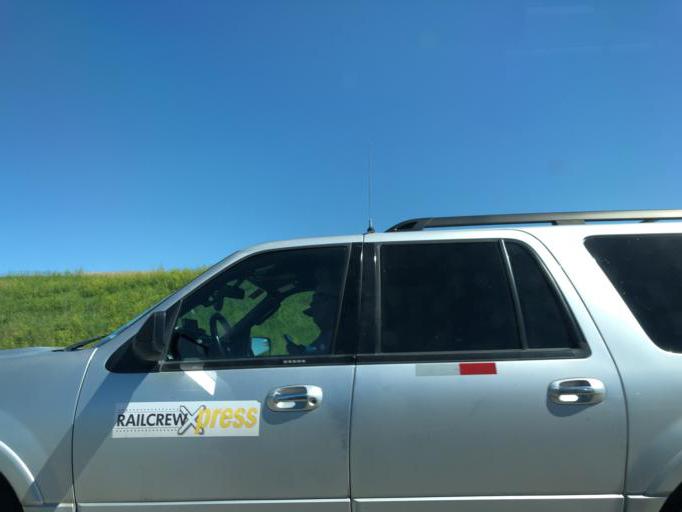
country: US
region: Nebraska
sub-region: Seward County
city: Milford
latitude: 40.8213
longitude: -96.9778
